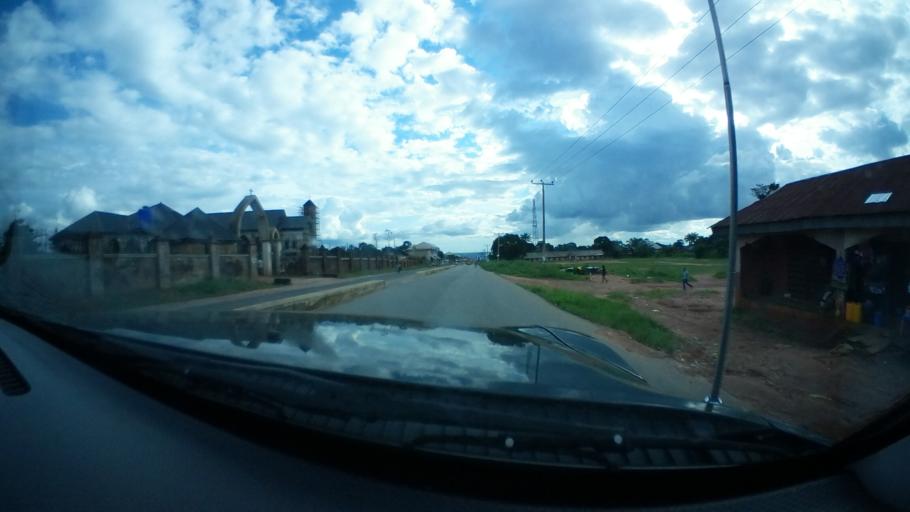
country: NG
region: Anambra
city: Uga
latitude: 5.8564
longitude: 7.1016
